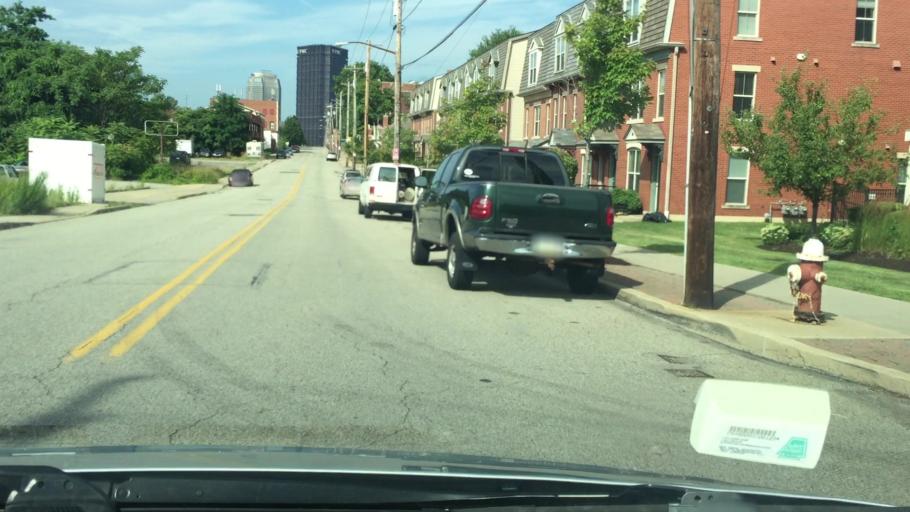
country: US
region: Pennsylvania
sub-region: Allegheny County
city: Pittsburgh
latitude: 40.4482
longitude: -79.9784
